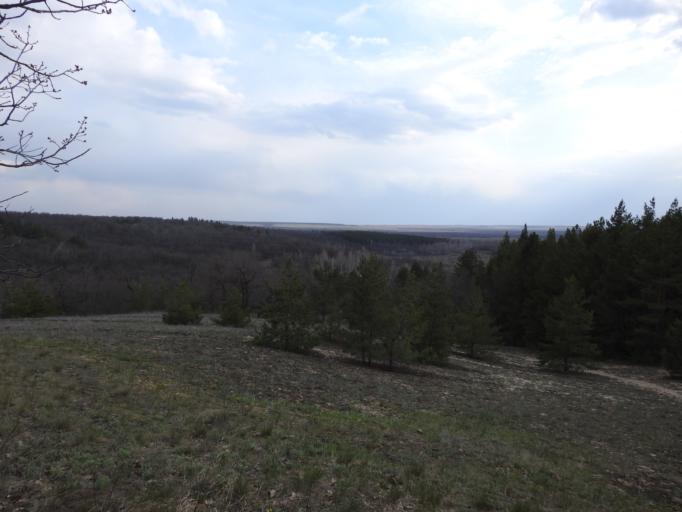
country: RU
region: Saratov
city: Krasnyy Oktyabr'
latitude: 51.4272
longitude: 45.5444
